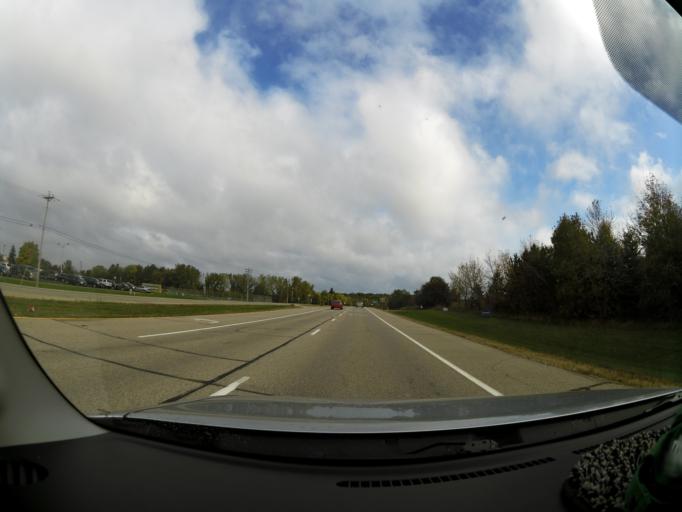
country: US
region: Minnesota
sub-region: Washington County
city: Lake Elmo
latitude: 44.9606
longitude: -92.8625
